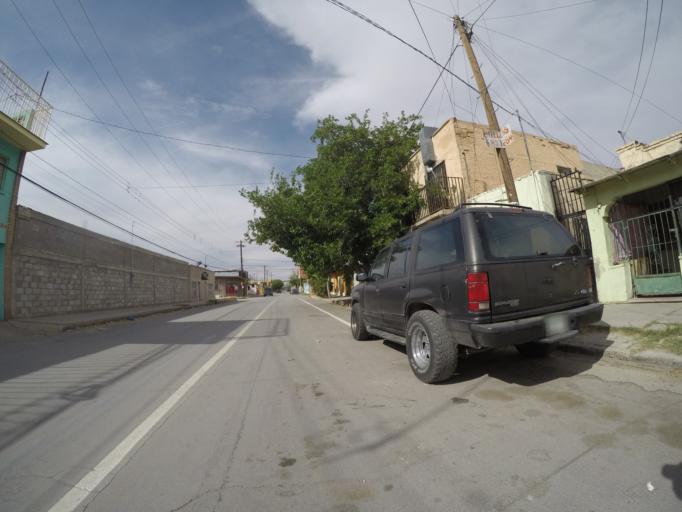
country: MX
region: Chihuahua
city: Ciudad Juarez
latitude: 31.7420
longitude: -106.4639
